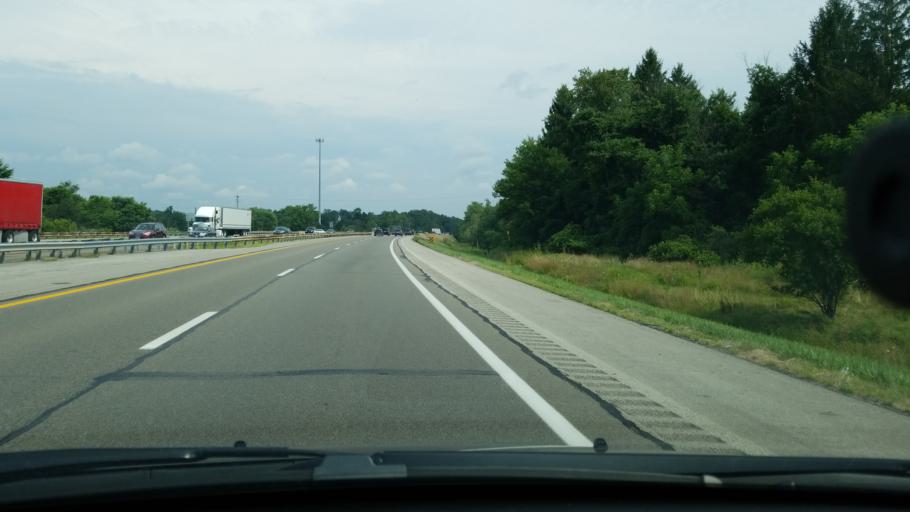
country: US
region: Ohio
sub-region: Mahoning County
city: New Middletown
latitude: 40.9159
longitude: -80.5272
